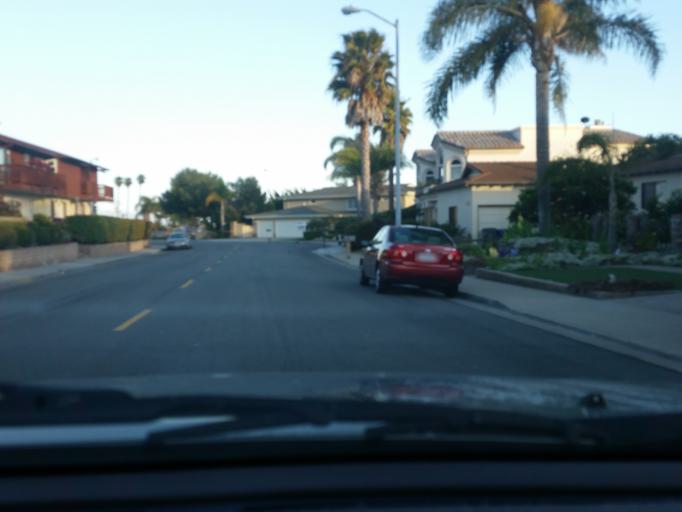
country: US
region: California
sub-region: San Luis Obispo County
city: Avila Beach
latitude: 35.1616
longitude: -120.6872
